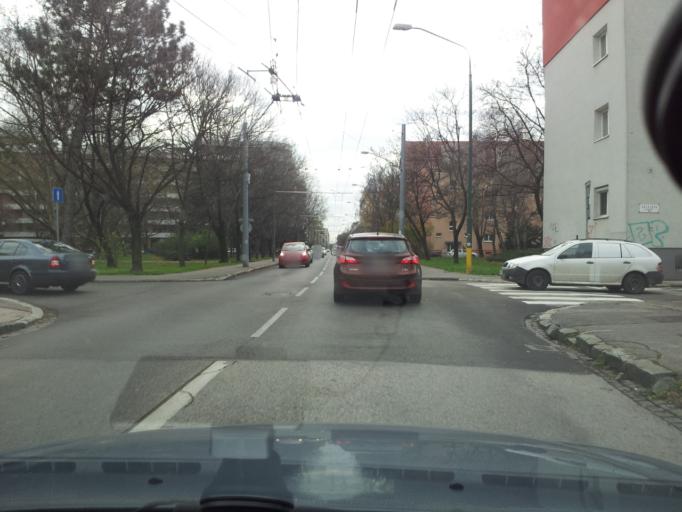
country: SK
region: Bratislavsky
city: Bratislava
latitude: 48.1534
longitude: 17.1288
